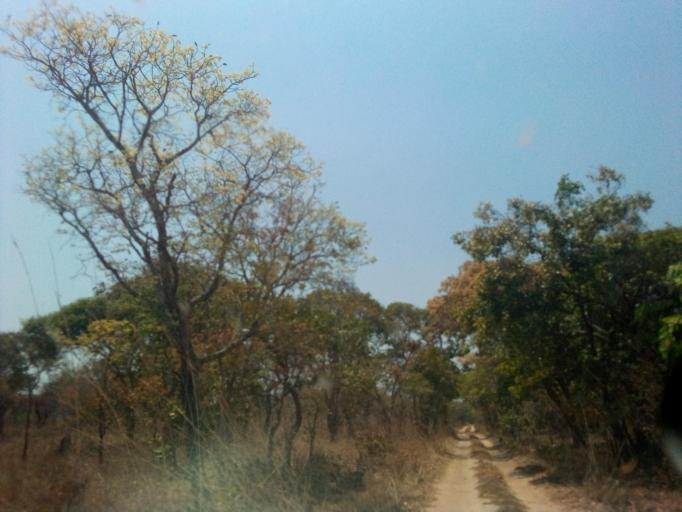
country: ZM
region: Copperbelt
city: Kataba
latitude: -12.2450
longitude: 30.3972
